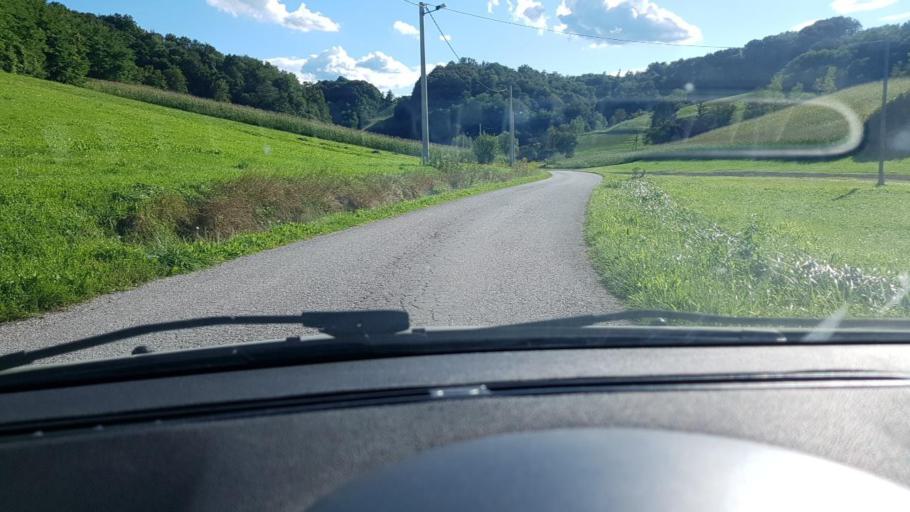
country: HR
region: Krapinsko-Zagorska
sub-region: Grad Krapina
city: Krapina
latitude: 46.1429
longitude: 15.8389
